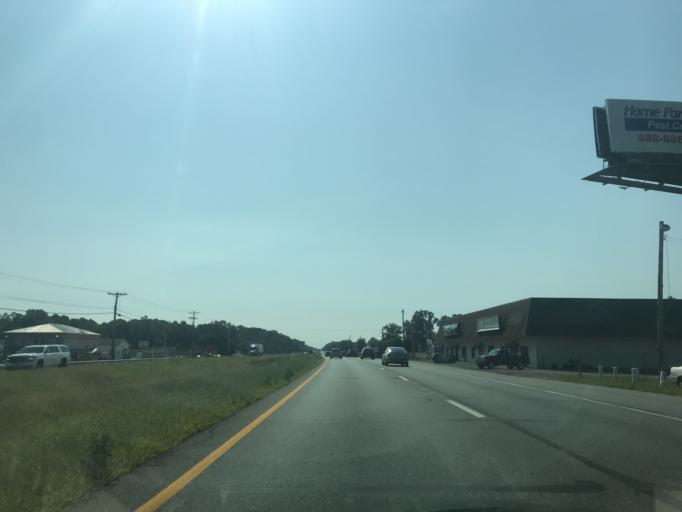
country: US
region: Maryland
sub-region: Saint Mary's County
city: Charlotte Hall
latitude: 38.4648
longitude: -76.7691
